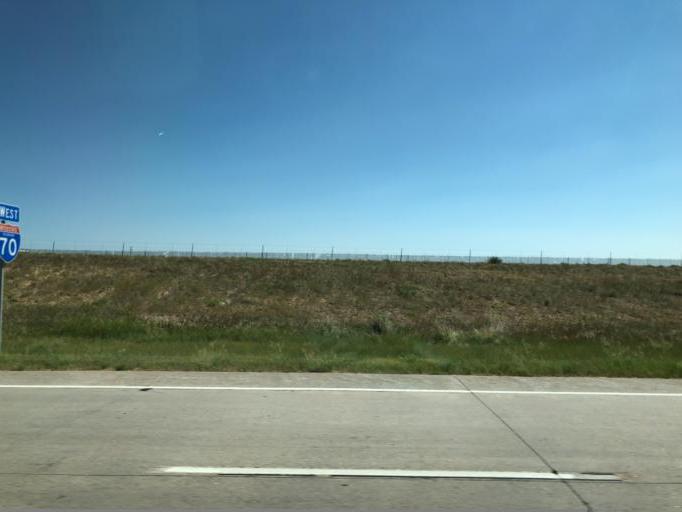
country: US
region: Colorado
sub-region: Lincoln County
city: Limon
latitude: 39.2698
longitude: -103.6763
